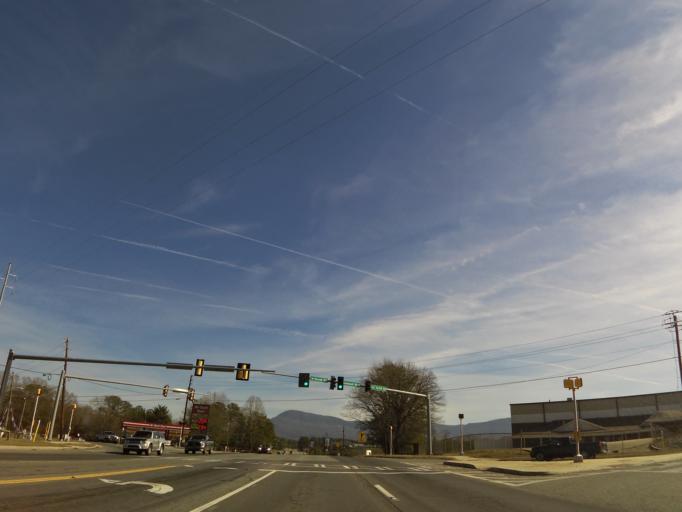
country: US
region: Georgia
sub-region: Murray County
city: Chatsworth
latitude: 34.7828
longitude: -84.7984
